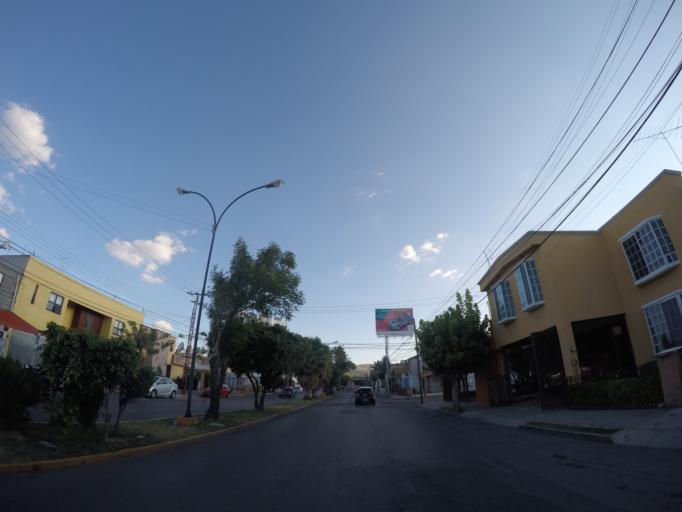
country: MX
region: San Luis Potosi
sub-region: San Luis Potosi
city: San Luis Potosi
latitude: 22.1358
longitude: -100.9888
